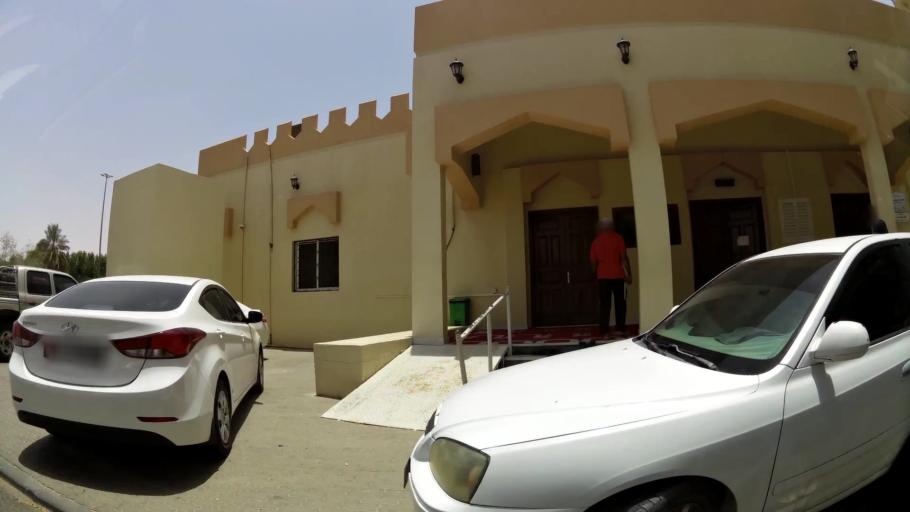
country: AE
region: Abu Dhabi
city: Al Ain
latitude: 24.2139
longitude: 55.7091
